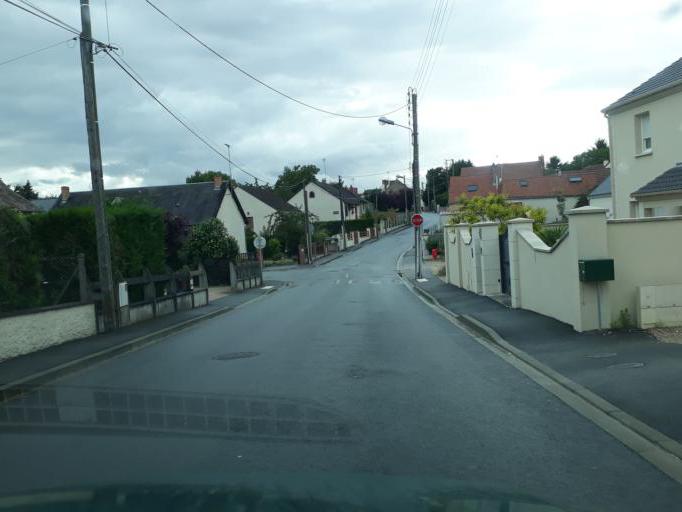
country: FR
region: Centre
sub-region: Departement du Loiret
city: La Chapelle-Saint-Mesmin
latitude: 47.8911
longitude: 1.8264
